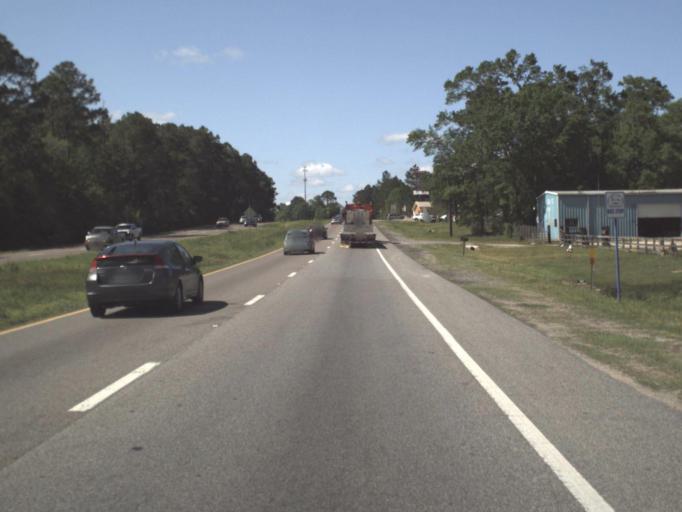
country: US
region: Florida
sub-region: Escambia County
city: Gonzalez
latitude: 30.5717
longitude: -87.2911
